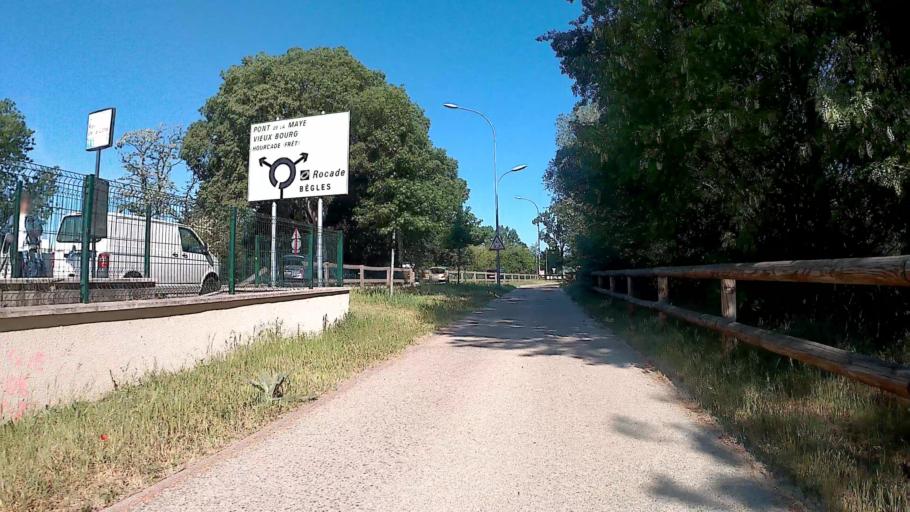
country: FR
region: Aquitaine
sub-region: Departement de la Gironde
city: Villenave-d'Ornon
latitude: 44.7808
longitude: -0.5358
